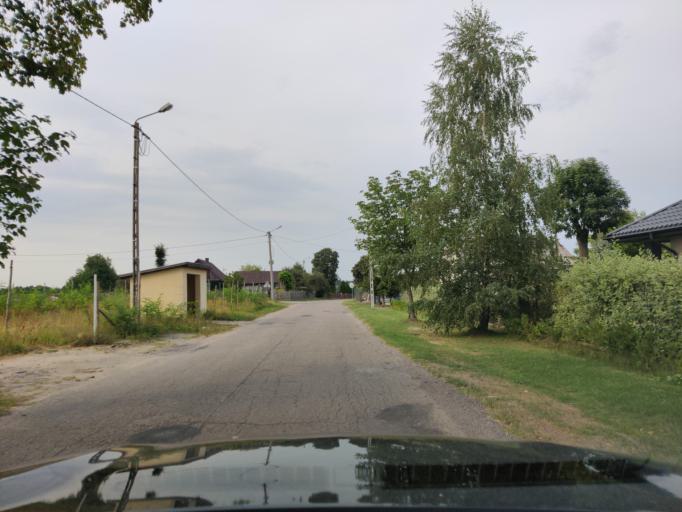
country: PL
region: Masovian Voivodeship
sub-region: Powiat pultuski
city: Obryte
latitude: 52.7404
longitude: 21.2519
